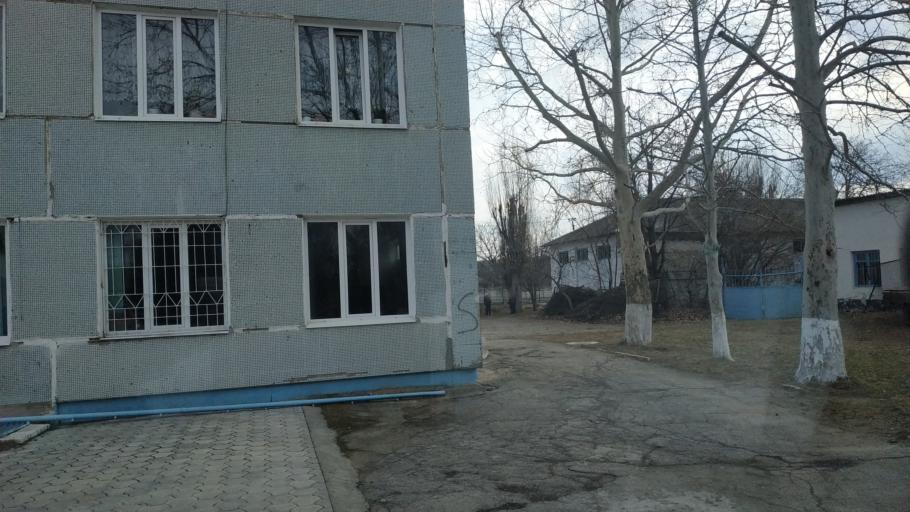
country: MD
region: Anenii Noi
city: Anenii Noi
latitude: 46.9007
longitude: 29.1388
